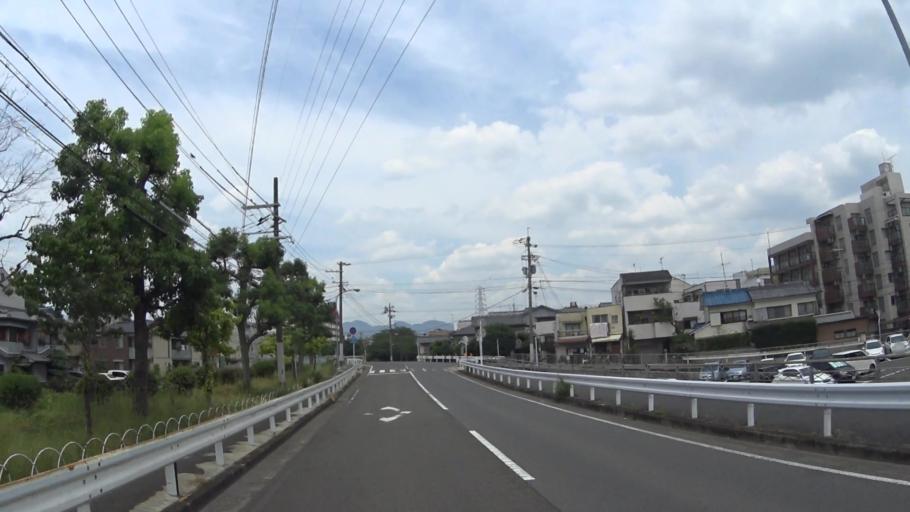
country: JP
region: Kyoto
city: Muko
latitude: 34.9936
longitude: 135.7172
